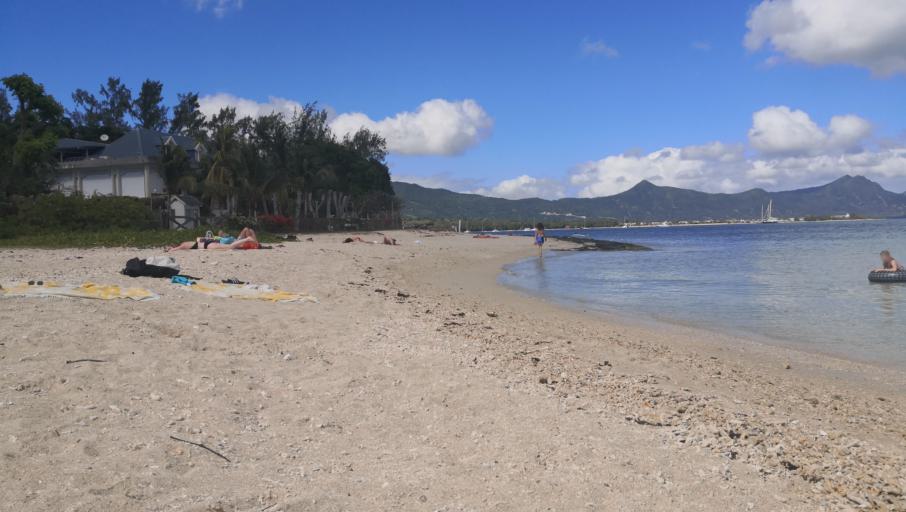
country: MU
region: Black River
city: Grande Riviere Noire
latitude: -20.3539
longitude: 57.3604
